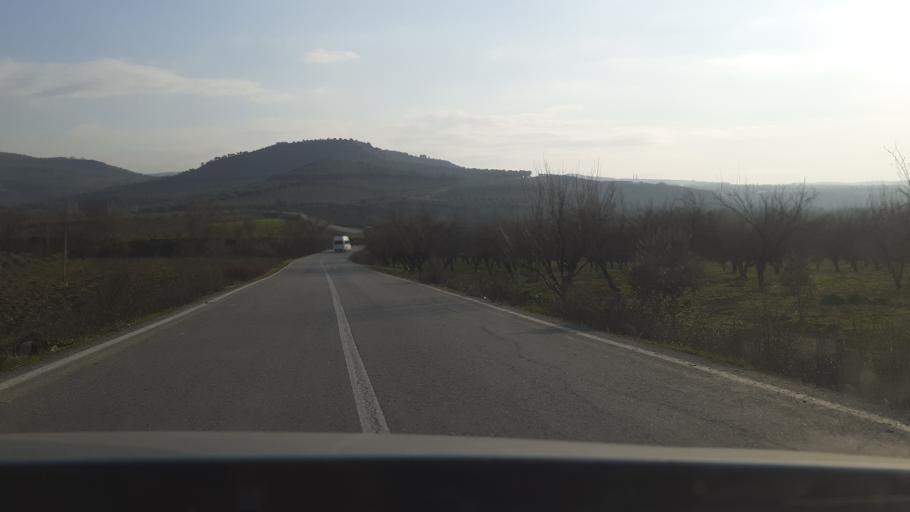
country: TR
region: Hatay
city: Oymakli
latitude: 36.1294
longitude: 36.3099
